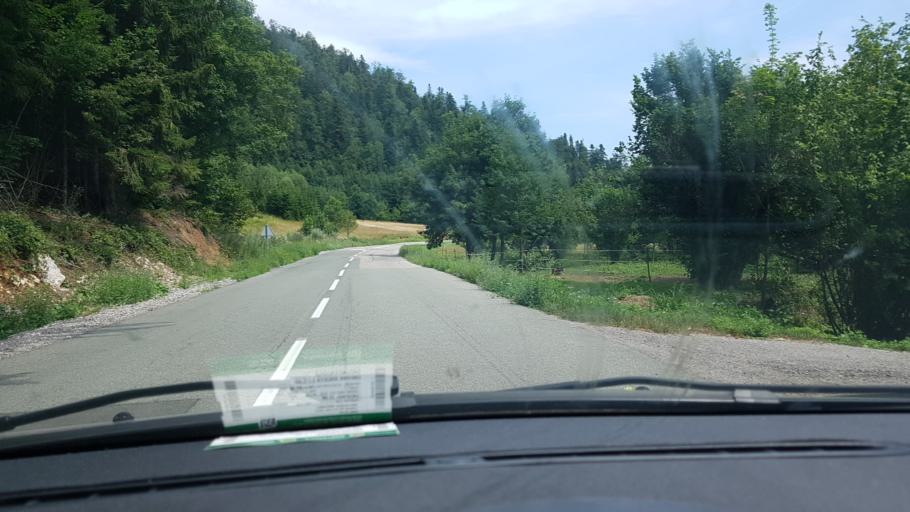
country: HR
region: Primorsko-Goranska
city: Hreljin
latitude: 45.3307
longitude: 14.6954
